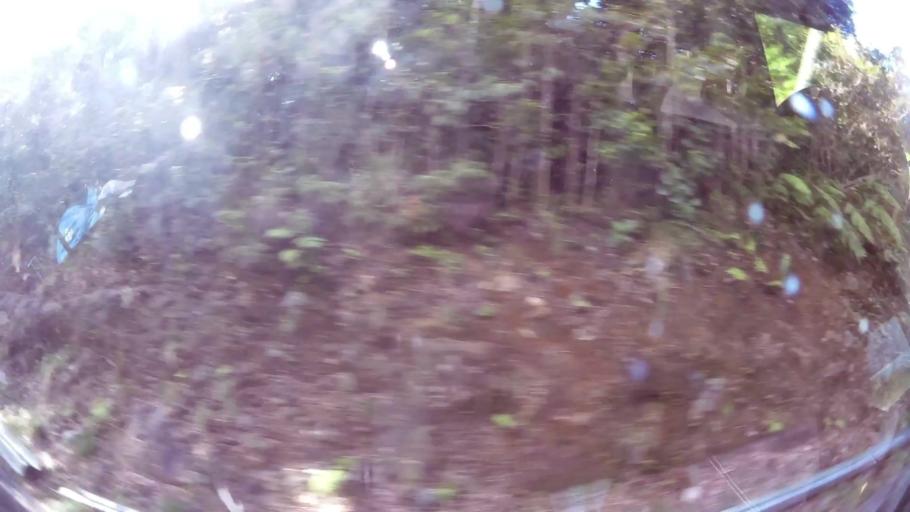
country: DM
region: Saint Paul
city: Pont Casse
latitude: 15.3704
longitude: -61.3514
